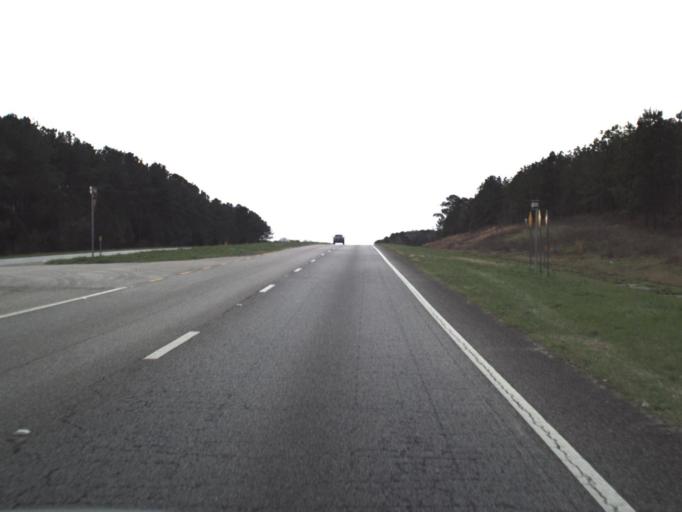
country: US
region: Florida
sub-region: Jackson County
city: Marianna
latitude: 30.8352
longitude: -85.3522
